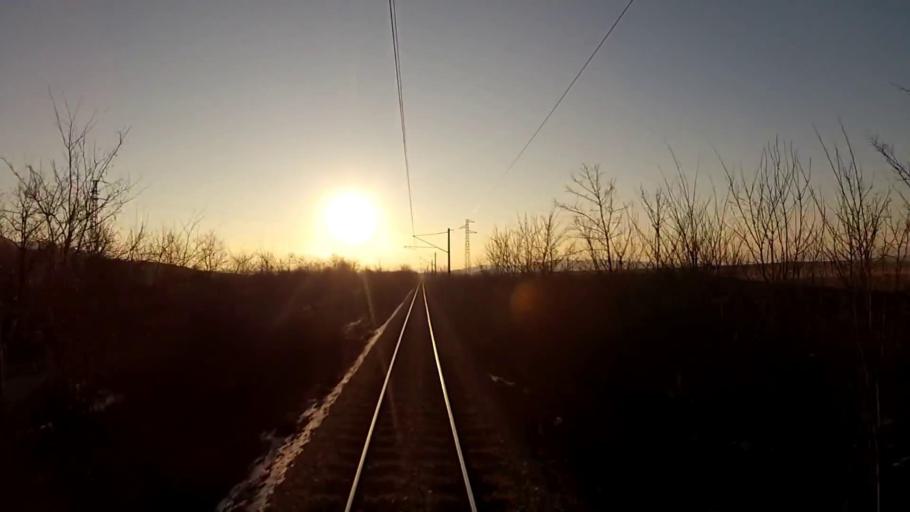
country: BG
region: Sofiya
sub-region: Obshtina Dragoman
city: Dragoman
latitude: 42.8932
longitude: 22.9716
